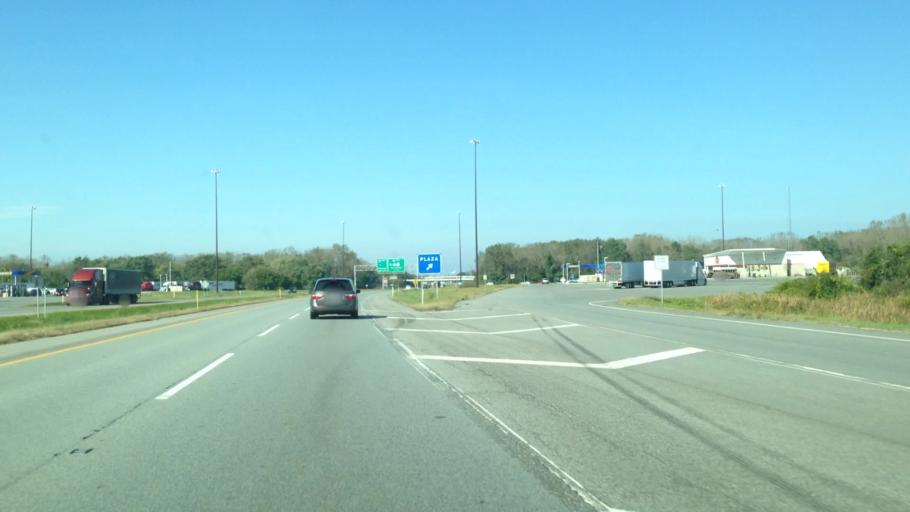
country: US
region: Indiana
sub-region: Lake County
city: Lake Station
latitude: 41.5872
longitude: -87.2139
